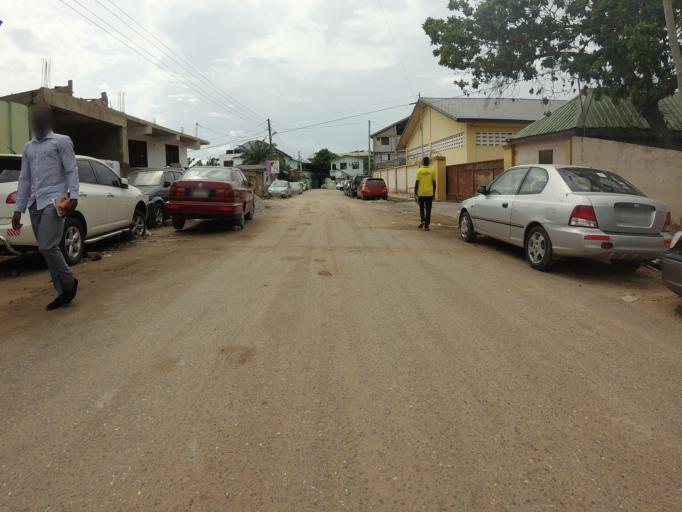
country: GH
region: Greater Accra
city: Accra
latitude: 5.5961
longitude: -0.2184
